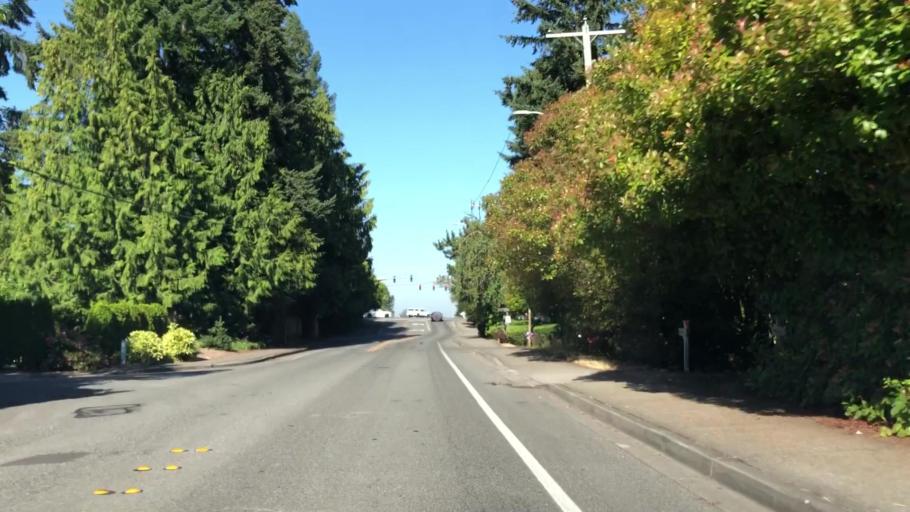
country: US
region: Washington
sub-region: King County
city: Eastgate
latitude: 47.6026
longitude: -122.1516
